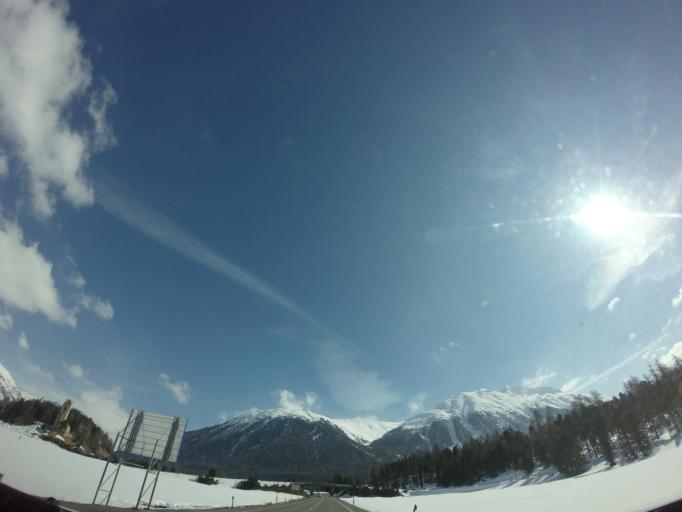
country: CH
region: Grisons
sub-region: Maloja District
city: Celerina
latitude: 46.5108
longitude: 9.8683
